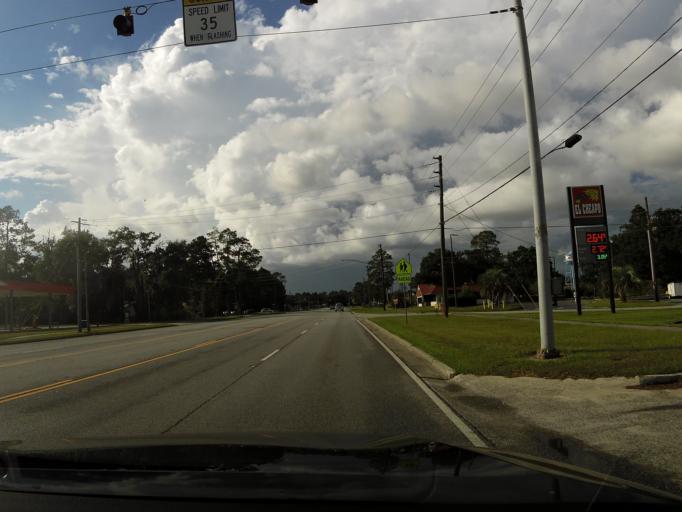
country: US
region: Georgia
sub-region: Liberty County
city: Hinesville
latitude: 31.8448
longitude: -81.6017
